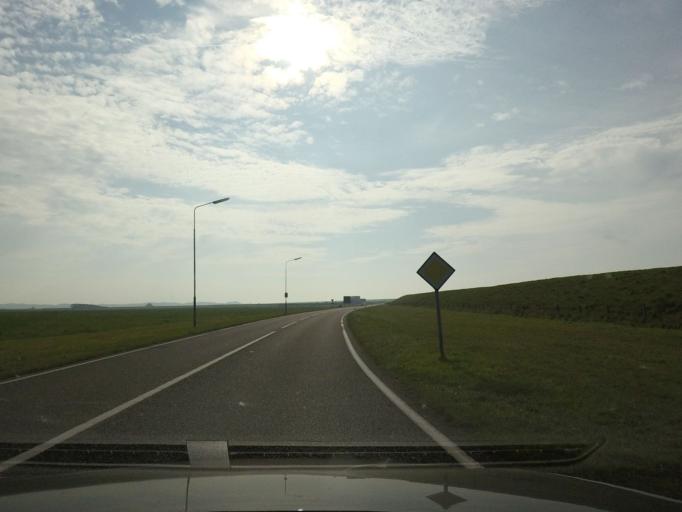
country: NL
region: North Holland
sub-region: Gemeente Schagen
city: Harenkarspel
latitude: 52.7598
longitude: 4.6602
